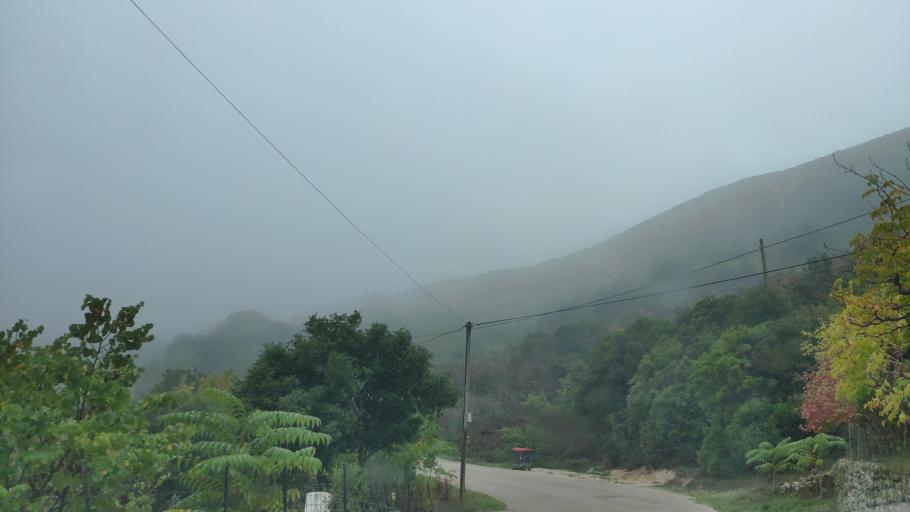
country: GR
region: Epirus
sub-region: Nomos Thesprotias
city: Paramythia
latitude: 39.4651
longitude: 20.6724
